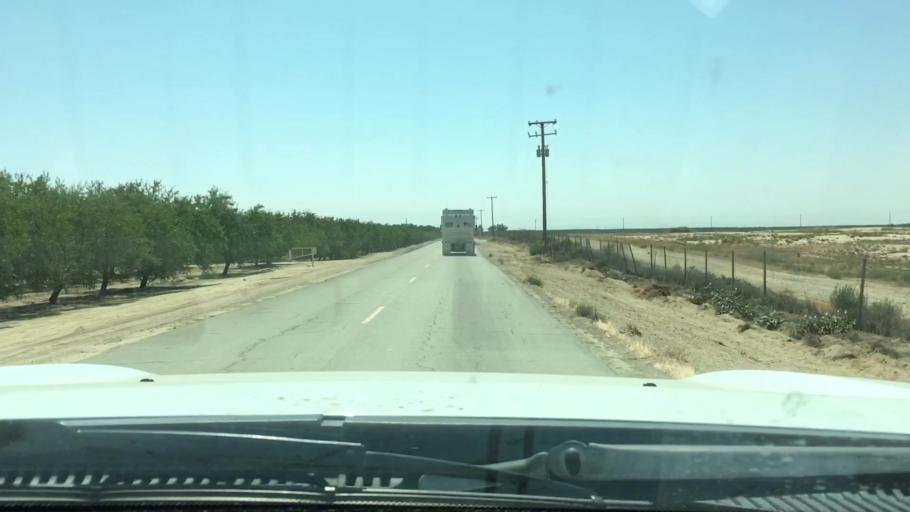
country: US
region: California
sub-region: Kern County
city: Wasco
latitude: 35.5119
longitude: -119.4033
